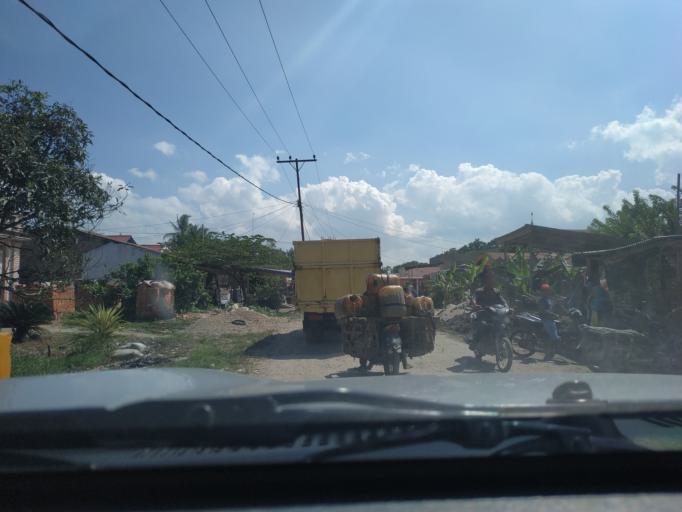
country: ID
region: North Sumatra
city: Tanjungbalai
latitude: 2.8731
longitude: 99.8600
